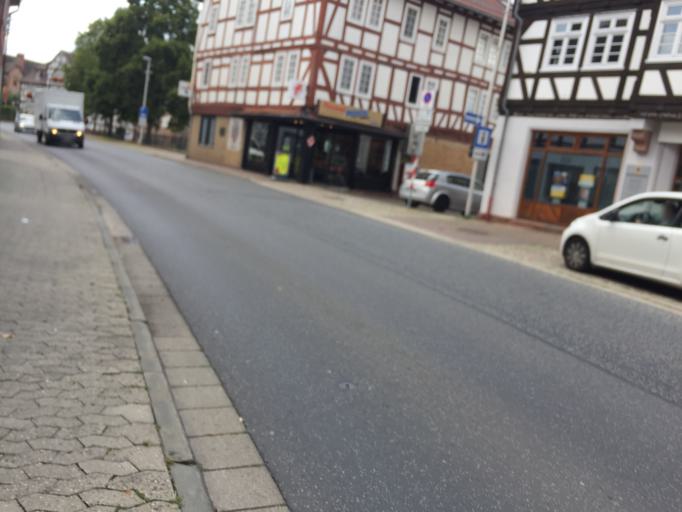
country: DE
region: Hesse
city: Schwalmstadt
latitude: 50.9110
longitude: 9.2360
